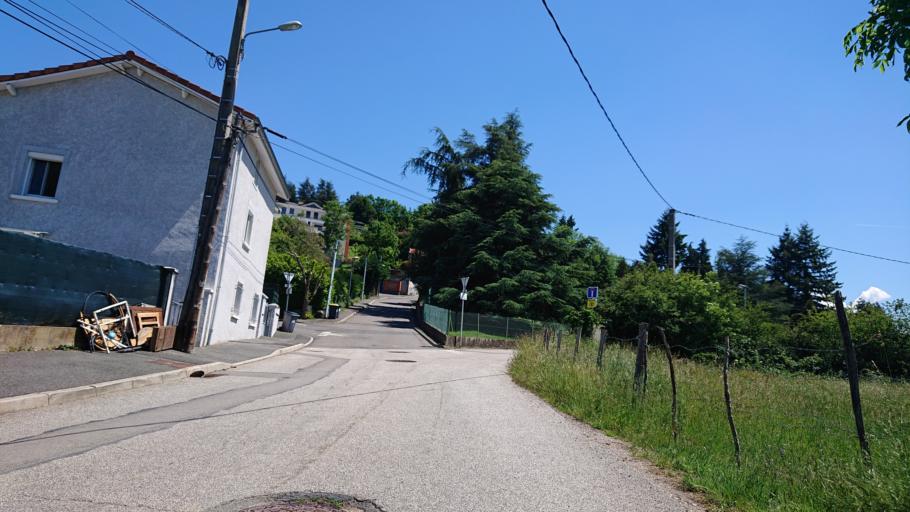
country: FR
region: Rhone-Alpes
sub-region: Departement de la Loire
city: Villars
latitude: 45.4626
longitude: 4.3455
